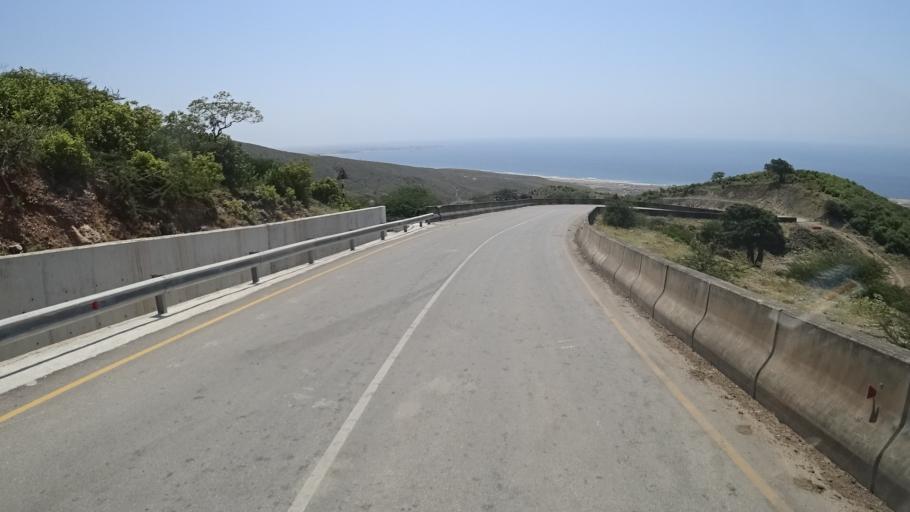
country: OM
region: Zufar
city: Salalah
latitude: 17.0520
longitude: 54.6105
